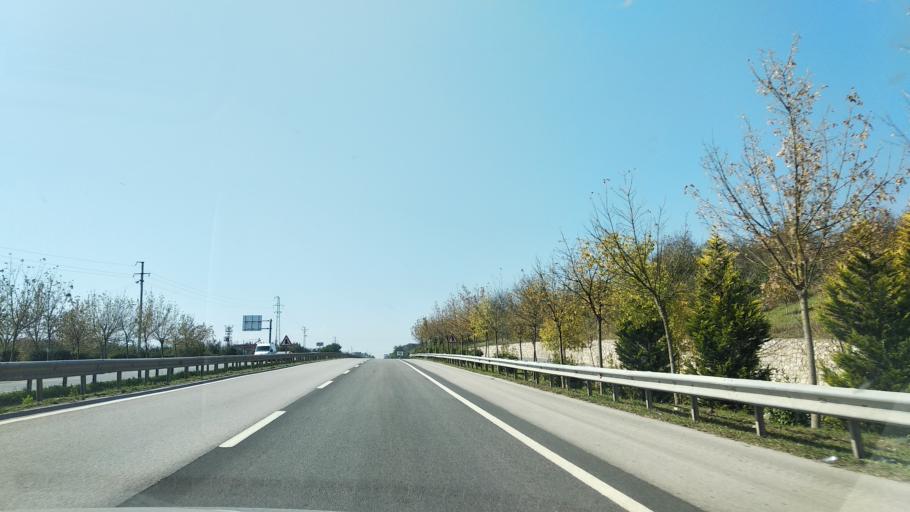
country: TR
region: Kocaeli
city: Derbent
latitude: 40.7319
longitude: 30.1795
